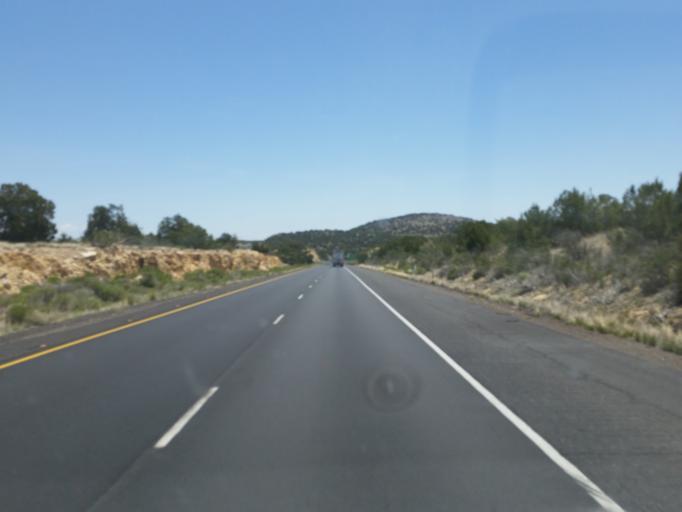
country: US
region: Arizona
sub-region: Coconino County
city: Flagstaff
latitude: 35.2013
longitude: -111.4316
